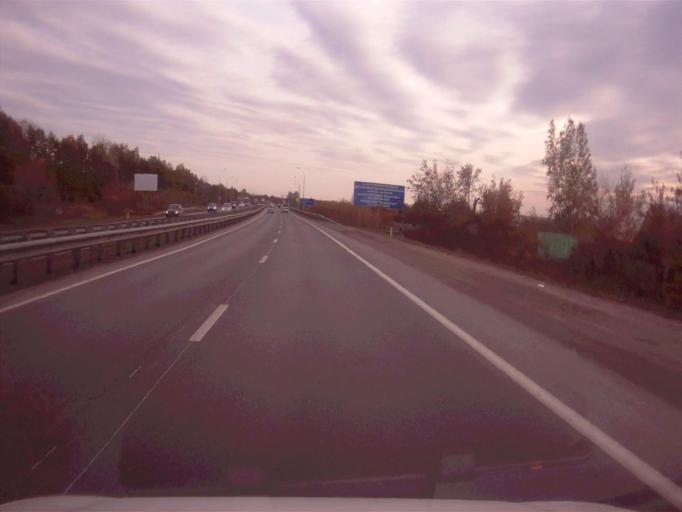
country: RU
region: Chelyabinsk
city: Novosineglazovskiy
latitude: 55.0347
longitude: 61.4426
